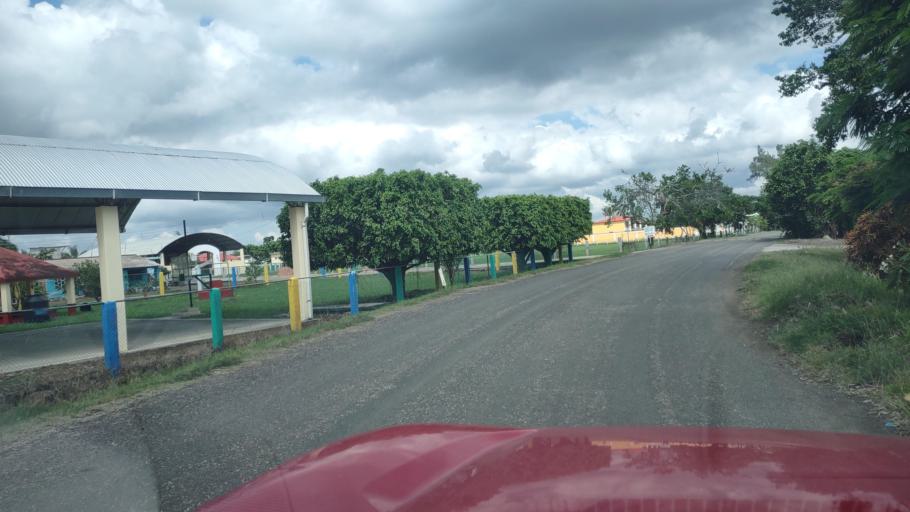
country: MX
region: Puebla
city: San Jose Acateno
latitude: 20.2732
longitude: -97.1300
